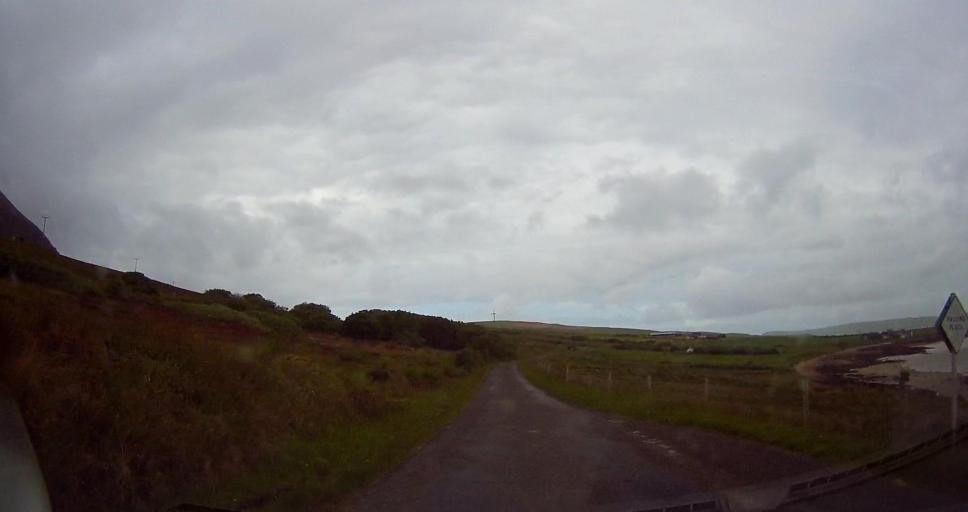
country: GB
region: Scotland
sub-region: Orkney Islands
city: Stromness
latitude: 58.9066
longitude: -3.3167
